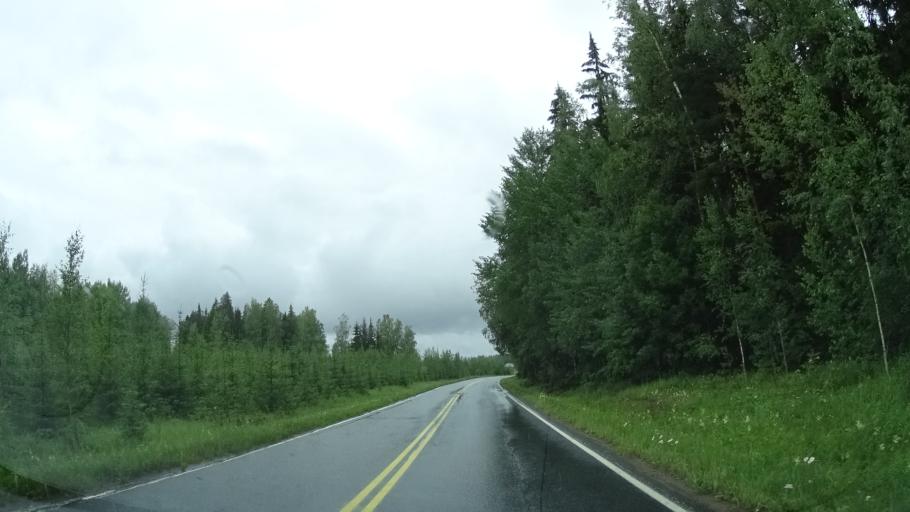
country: FI
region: Haeme
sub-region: Forssa
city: Humppila
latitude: 60.9925
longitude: 23.2565
